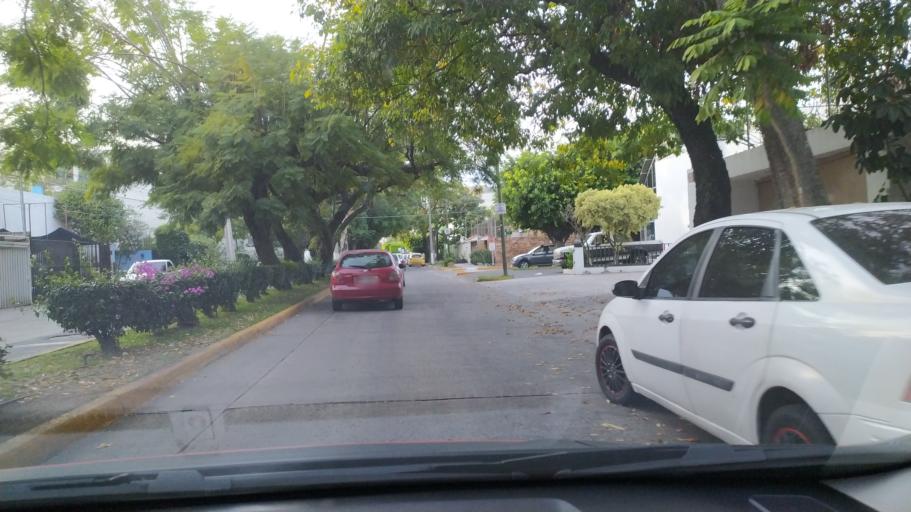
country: MX
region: Jalisco
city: Guadalajara
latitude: 20.6574
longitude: -103.3995
